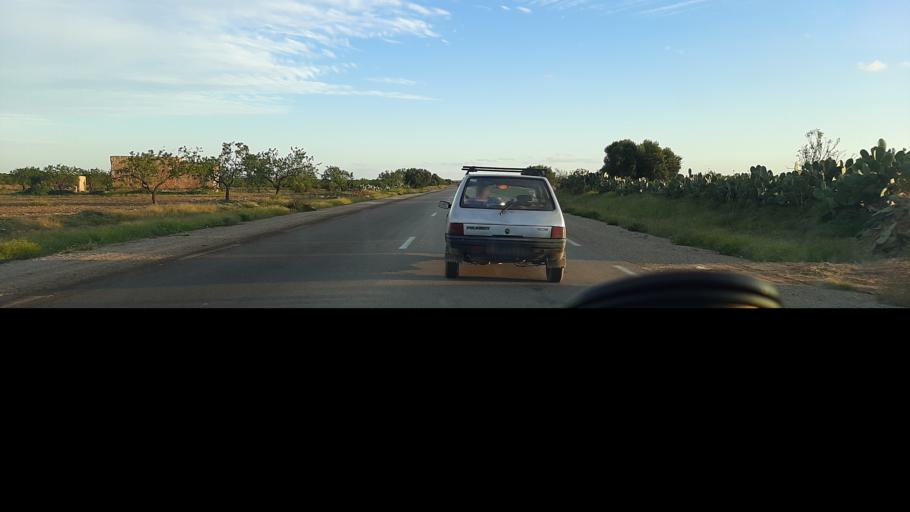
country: TN
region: Safaqis
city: Sfax
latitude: 34.9150
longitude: 10.6308
